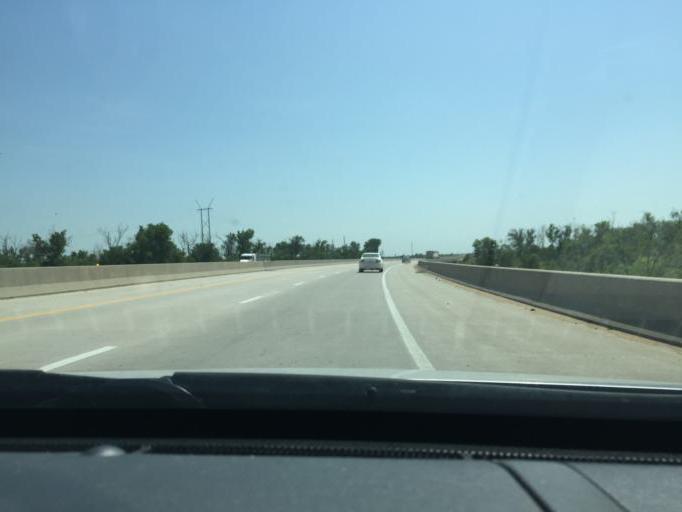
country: US
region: Kansas
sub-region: Reno County
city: South Hutchinson
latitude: 38.0179
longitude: -97.9128
